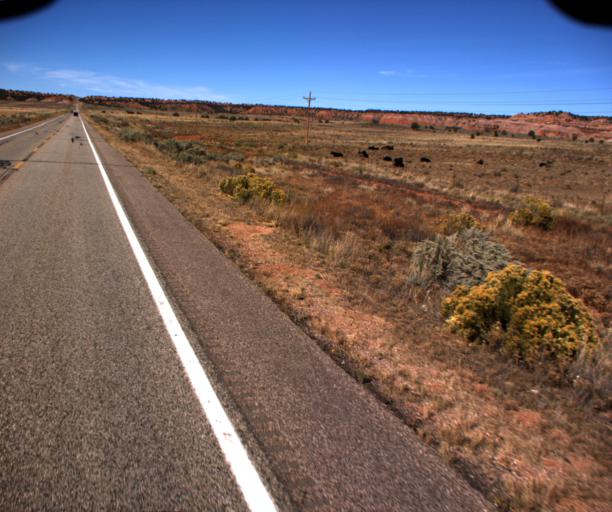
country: US
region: Arizona
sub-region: Mohave County
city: Colorado City
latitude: 36.8739
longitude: -112.8677
